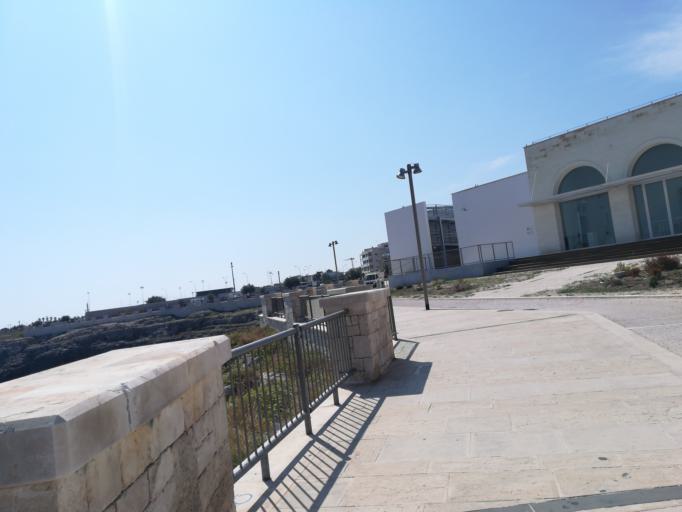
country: IT
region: Apulia
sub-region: Provincia di Bari
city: Polignano a Mare
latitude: 40.9945
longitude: 17.2287
